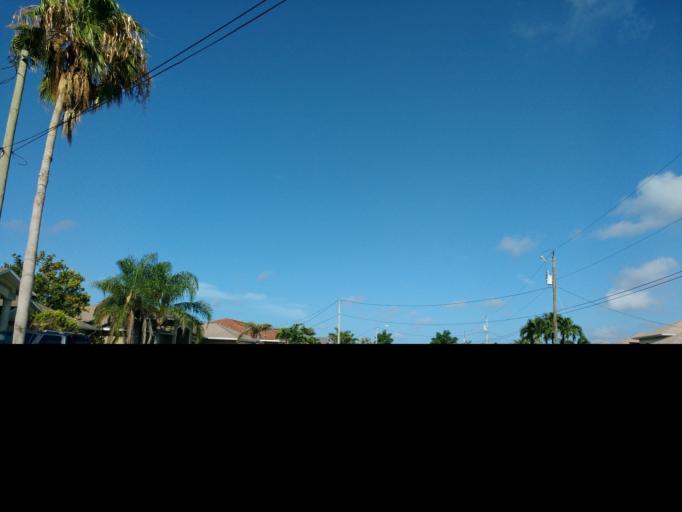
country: US
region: Florida
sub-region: Lee County
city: Cape Coral
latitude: 26.5862
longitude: -82.0258
